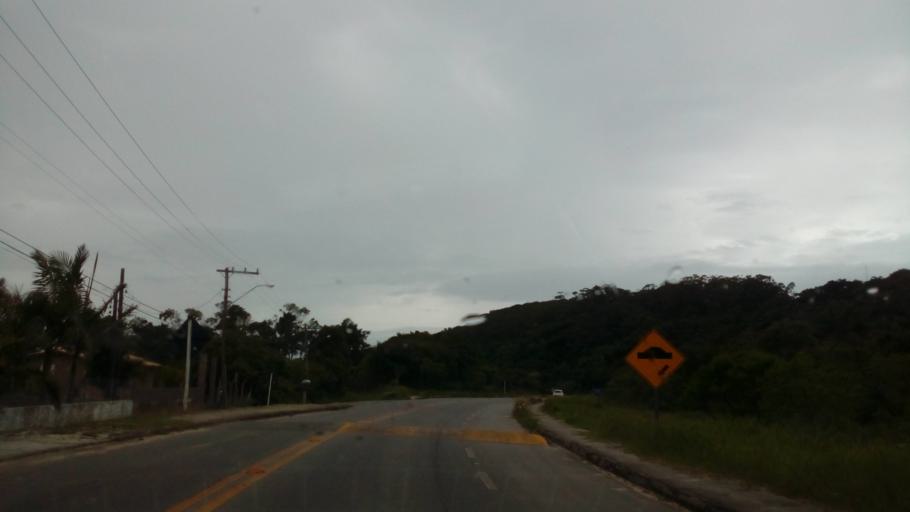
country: BR
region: Santa Catarina
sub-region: Laguna
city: Laguna
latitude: -28.5155
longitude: -48.7690
